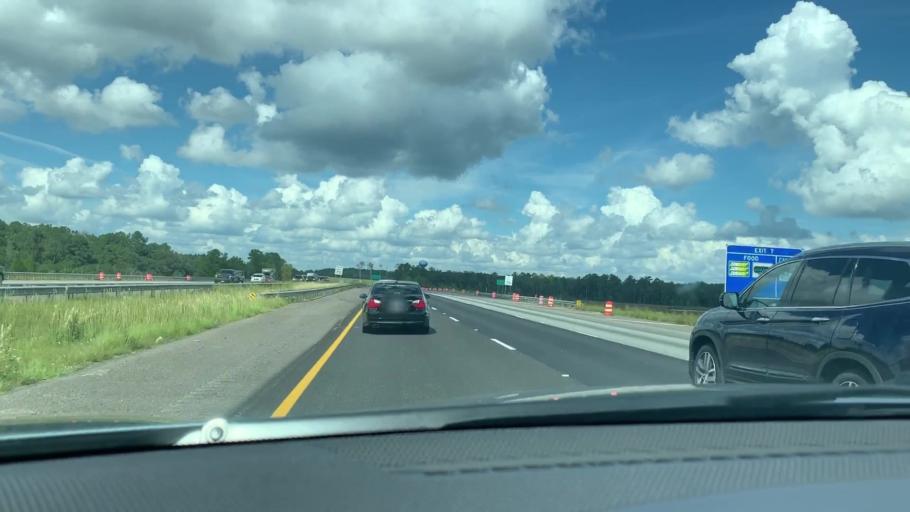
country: US
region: Georgia
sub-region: Camden County
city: Kingsland
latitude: 30.8373
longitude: -81.6690
